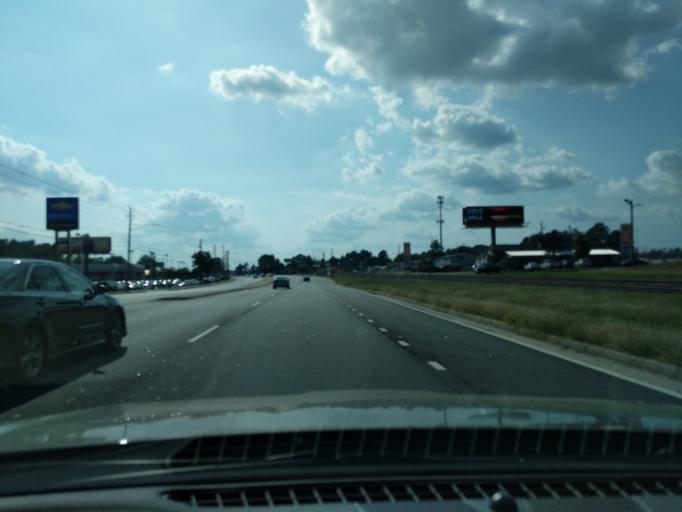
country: US
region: Georgia
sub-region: Columbia County
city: Martinez
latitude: 33.5164
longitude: -82.0745
